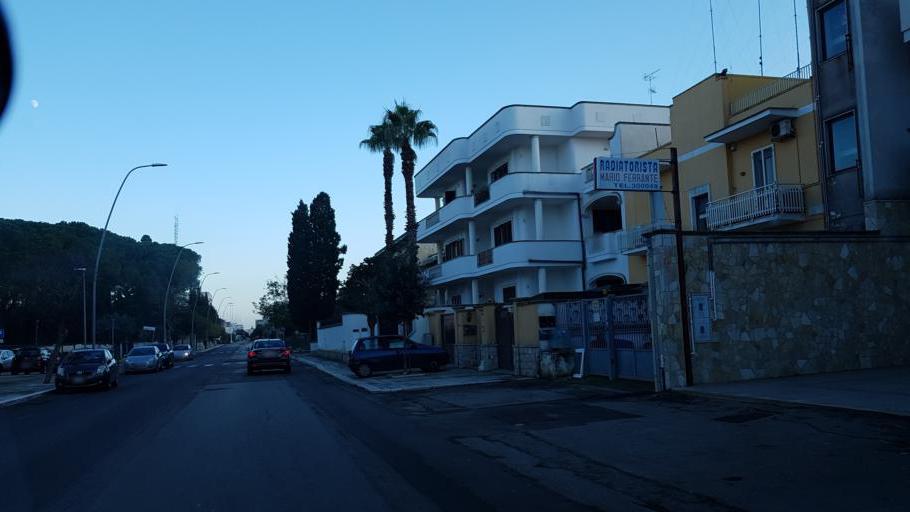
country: IT
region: Apulia
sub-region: Provincia di Lecce
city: Lecce
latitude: 40.3615
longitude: 18.1542
